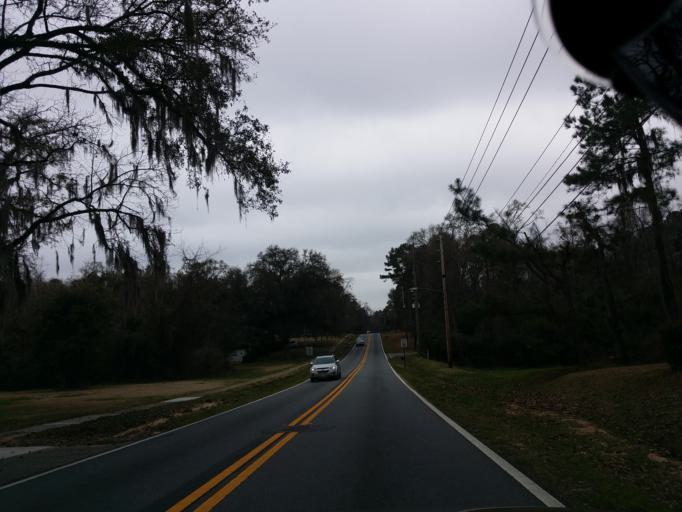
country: US
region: Florida
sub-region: Leon County
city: Tallahassee
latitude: 30.4921
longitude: -84.2300
